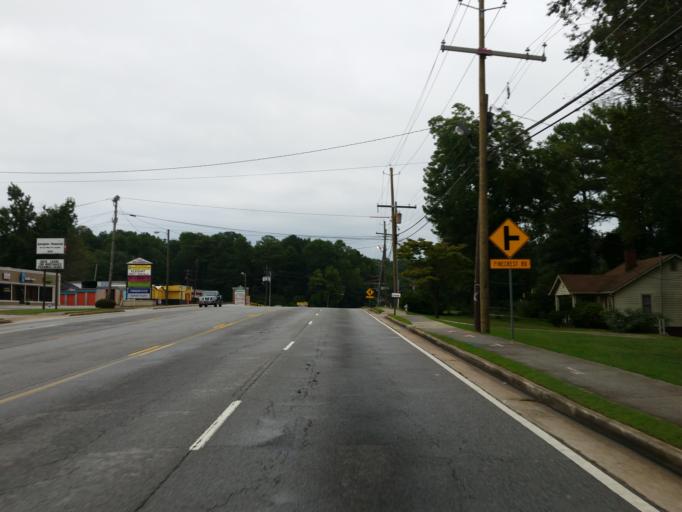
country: US
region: Georgia
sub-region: Cobb County
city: Austell
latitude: 33.8174
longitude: -84.6095
